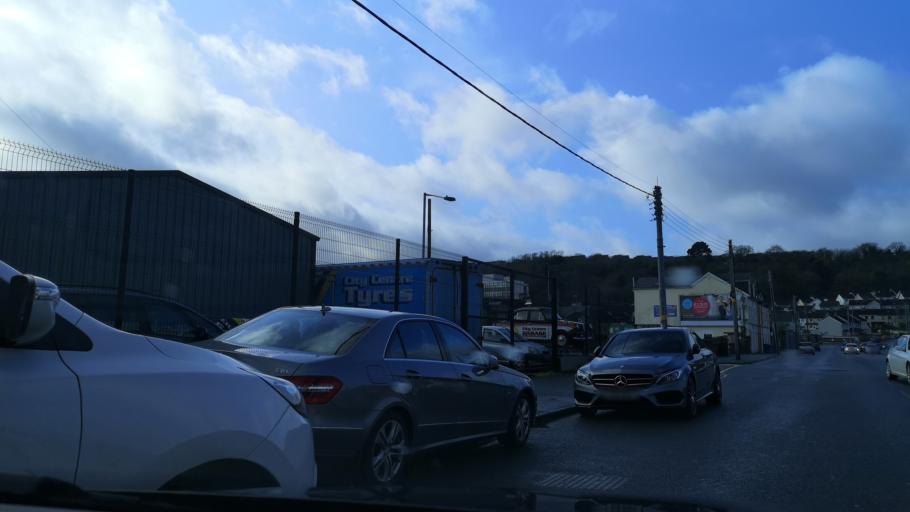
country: GB
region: Northern Ireland
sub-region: Newry and Mourne District
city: Newry
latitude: 54.1783
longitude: -6.3436
